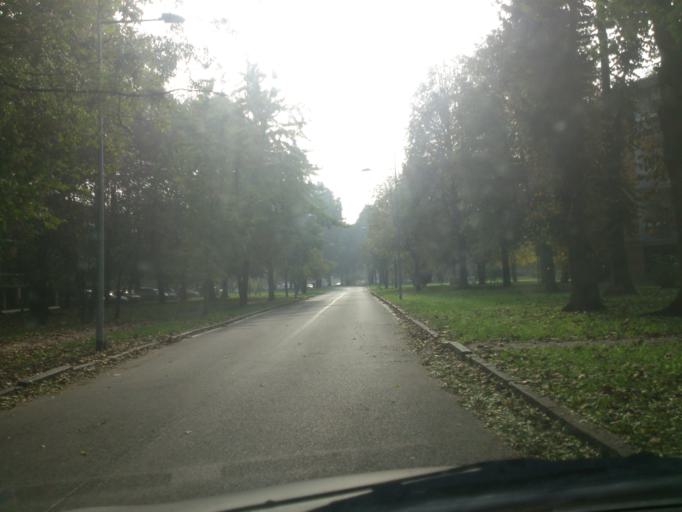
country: IT
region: Lombardy
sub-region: Citta metropolitana di Milano
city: San Donato Milanese
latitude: 45.4196
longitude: 9.2811
